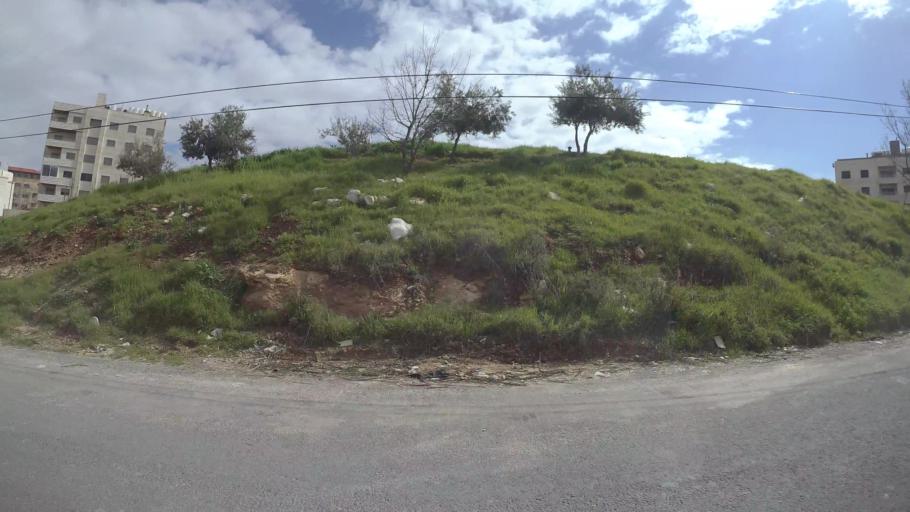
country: JO
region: Amman
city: Al Jubayhah
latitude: 31.9983
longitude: 35.8325
